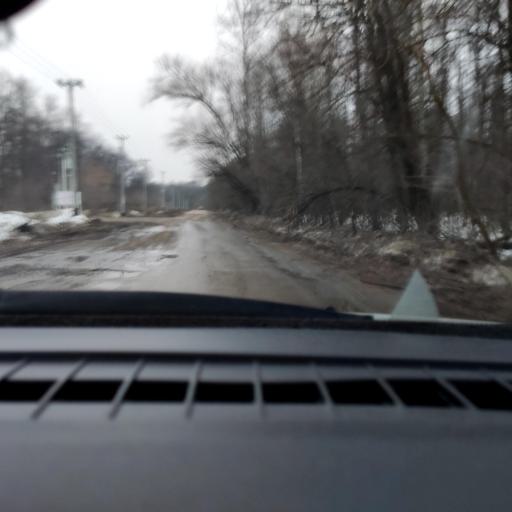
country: RU
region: Samara
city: Novosemeykino
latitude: 53.3325
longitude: 50.2726
